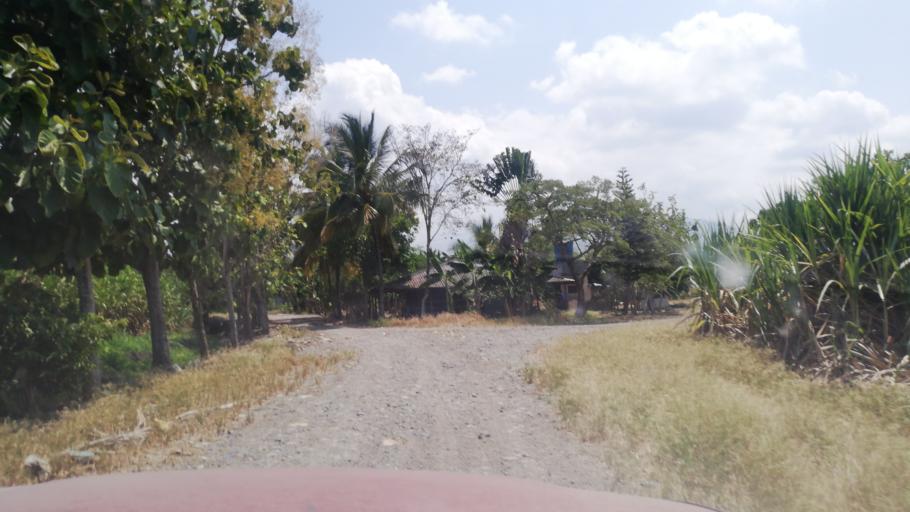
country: CO
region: Valle del Cauca
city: San Pedro
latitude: 3.9923
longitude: -76.2648
